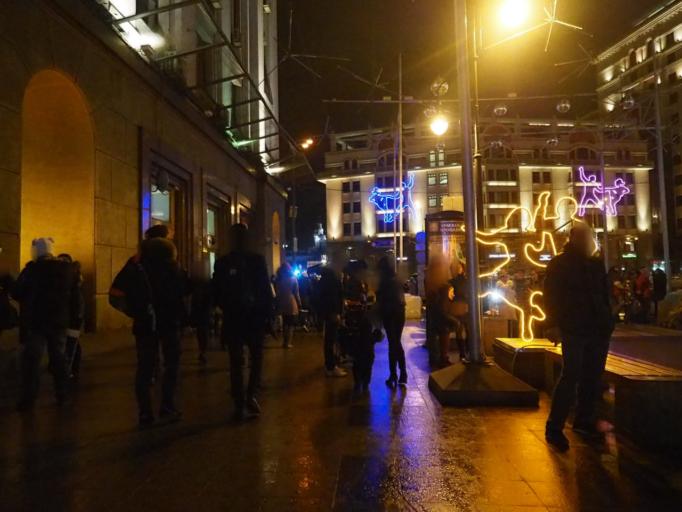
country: RU
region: Moscow
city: Moscow
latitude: 55.7589
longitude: 37.6174
